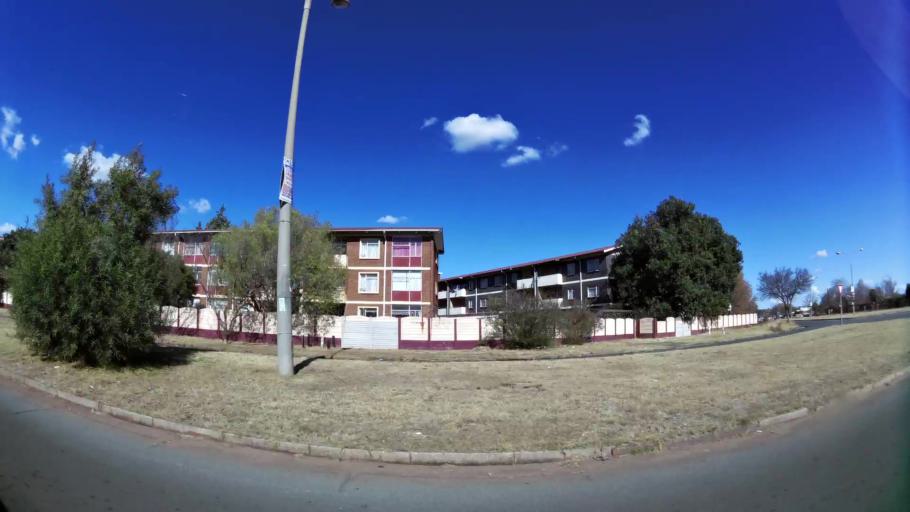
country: ZA
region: Gauteng
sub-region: West Rand District Municipality
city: Carletonville
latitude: -26.3600
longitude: 27.3950
